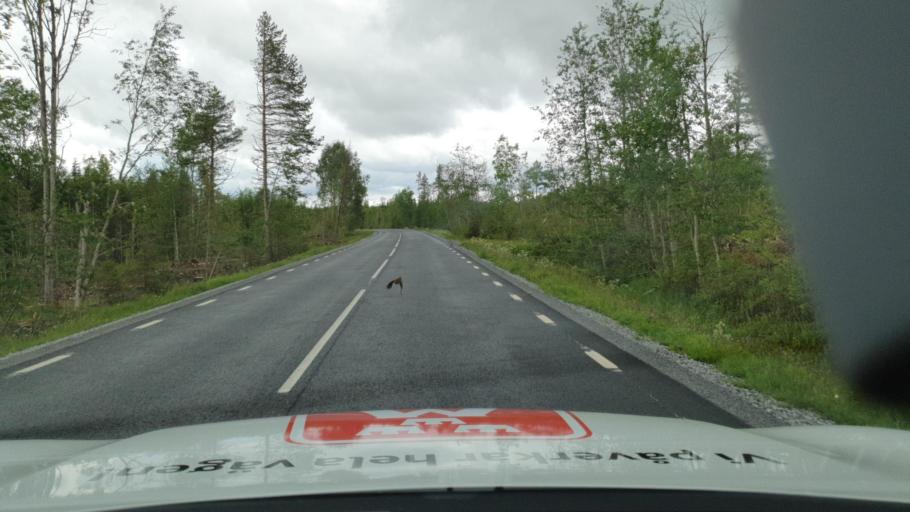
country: SE
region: Vaesterbotten
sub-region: Dorotea Kommun
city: Dorotea
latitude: 64.2441
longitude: 16.5348
